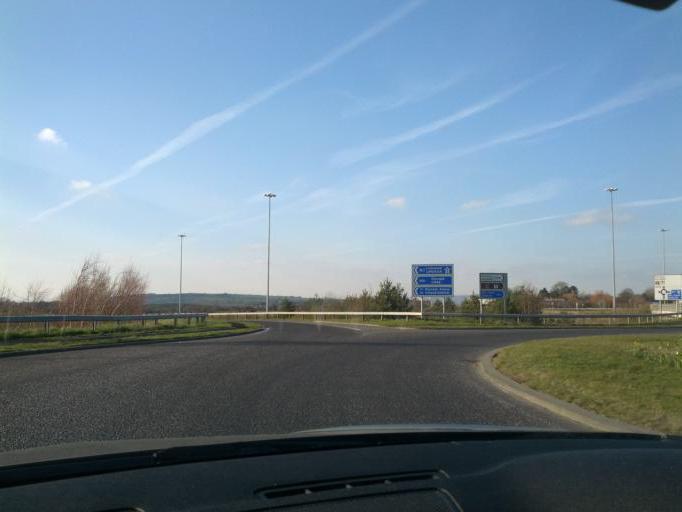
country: IE
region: Leinster
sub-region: Kildare
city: Kildare
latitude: 53.1509
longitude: -6.9195
